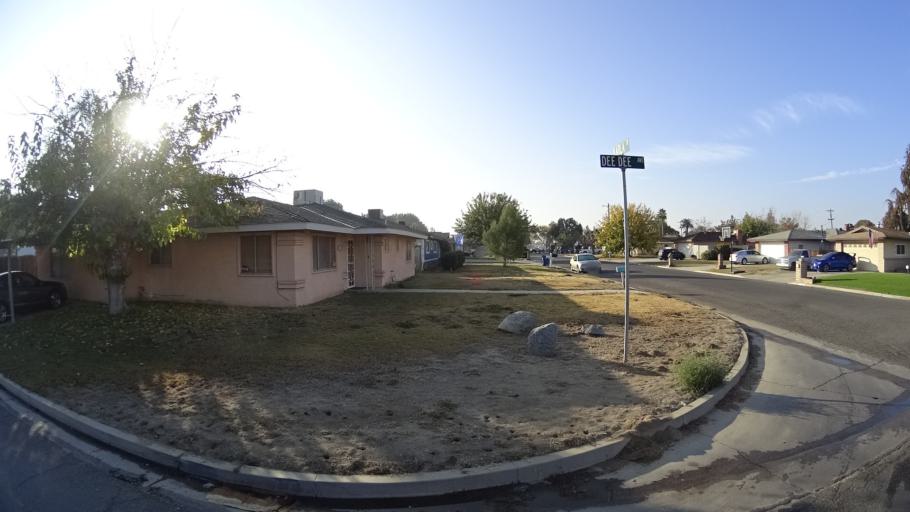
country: US
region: California
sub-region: Kern County
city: Greenacres
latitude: 35.3861
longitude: -119.1203
